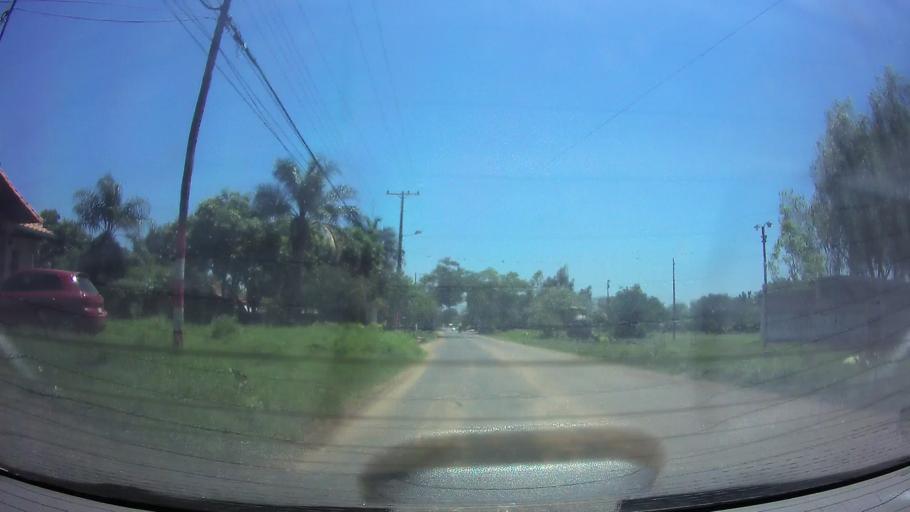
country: PY
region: Central
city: San Lorenzo
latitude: -25.3263
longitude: -57.4847
